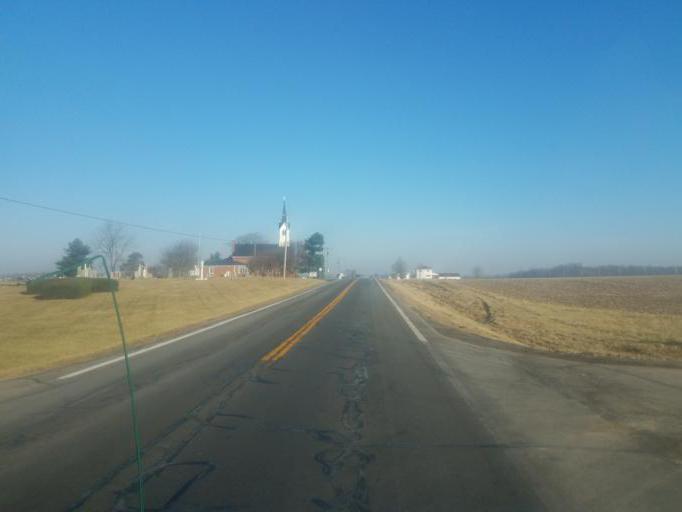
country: US
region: Ohio
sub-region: Crawford County
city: Bucyrus
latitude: 40.9794
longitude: -82.9298
